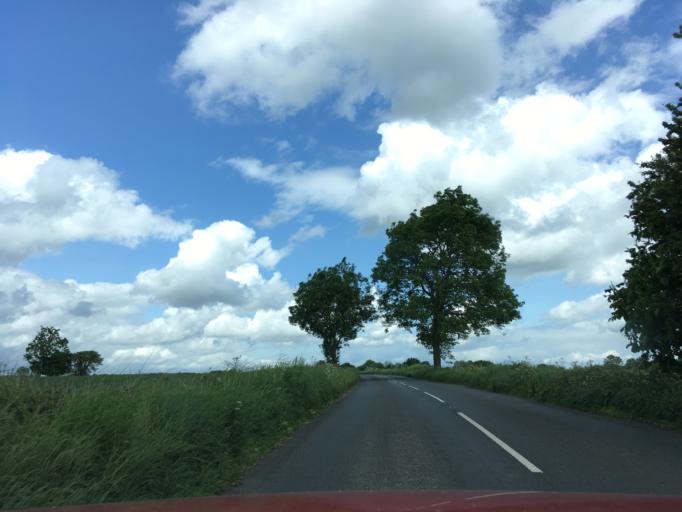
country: GB
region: England
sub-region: Gloucestershire
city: Shurdington
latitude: 51.7952
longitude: -2.1273
